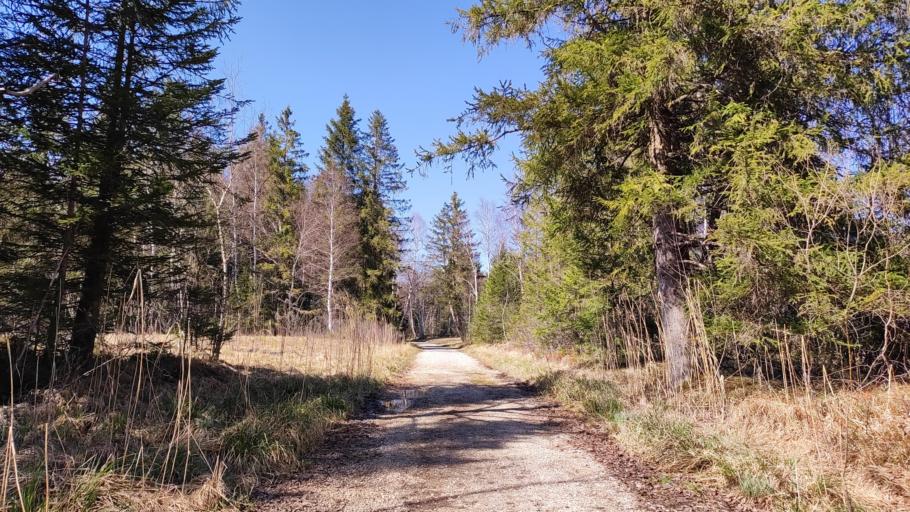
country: DE
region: Bavaria
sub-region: Upper Bavaria
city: Unterammergau
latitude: 47.6350
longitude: 11.0261
